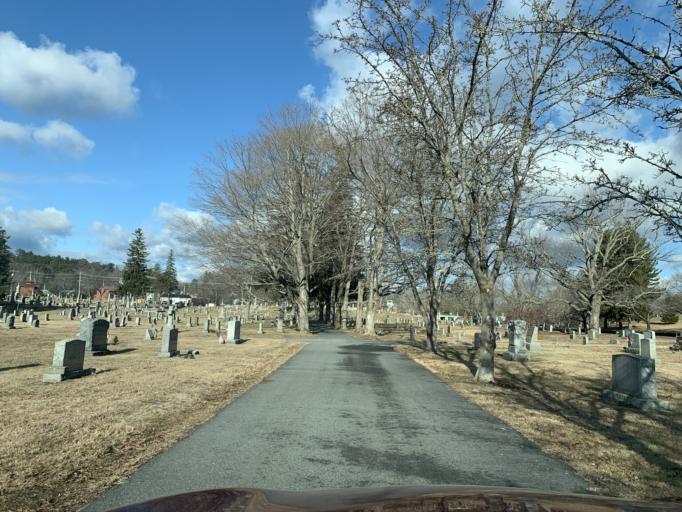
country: US
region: Massachusetts
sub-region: Essex County
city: Amesbury
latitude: 42.8438
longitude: -70.9345
